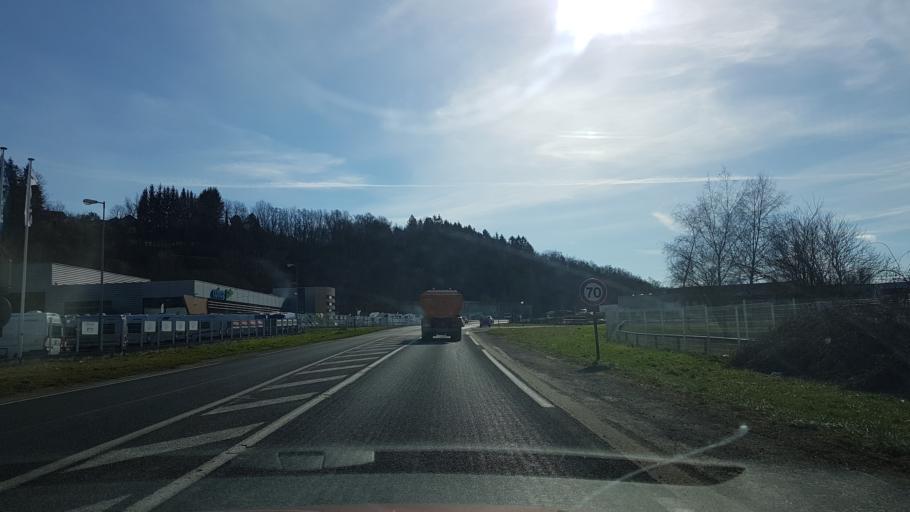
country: FR
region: Rhone-Alpes
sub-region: Departement de la Haute-Savoie
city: La Balme-de-Sillingy
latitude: 45.9762
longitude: 6.0310
